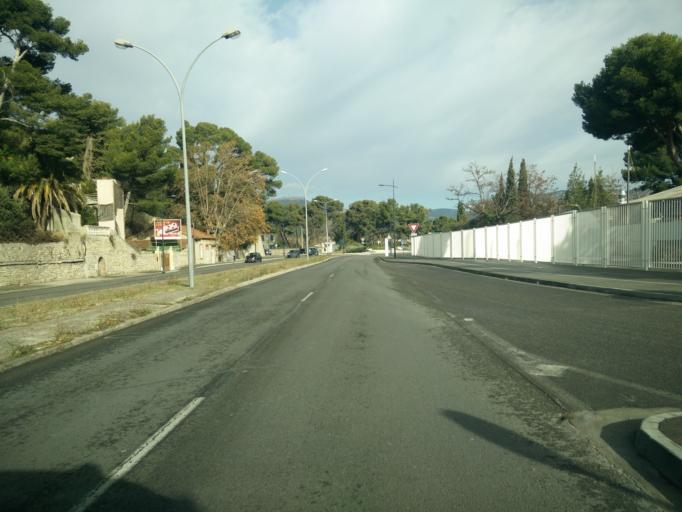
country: FR
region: Provence-Alpes-Cote d'Azur
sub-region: Departement du Var
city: La Seyne-sur-Mer
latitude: 43.1119
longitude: 5.8831
